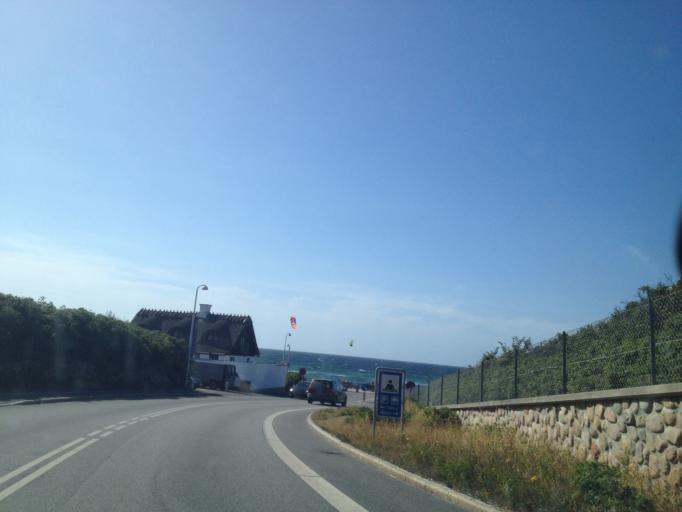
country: DK
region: Capital Region
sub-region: Gribskov Kommune
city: Helsinge
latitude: 56.0990
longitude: 12.1633
